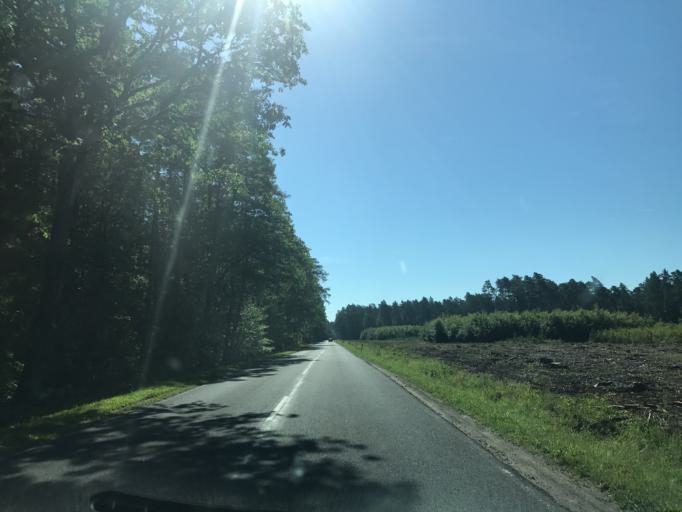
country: PL
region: Pomeranian Voivodeship
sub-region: Powiat slupski
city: Potegowo
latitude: 54.4033
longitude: 17.4545
